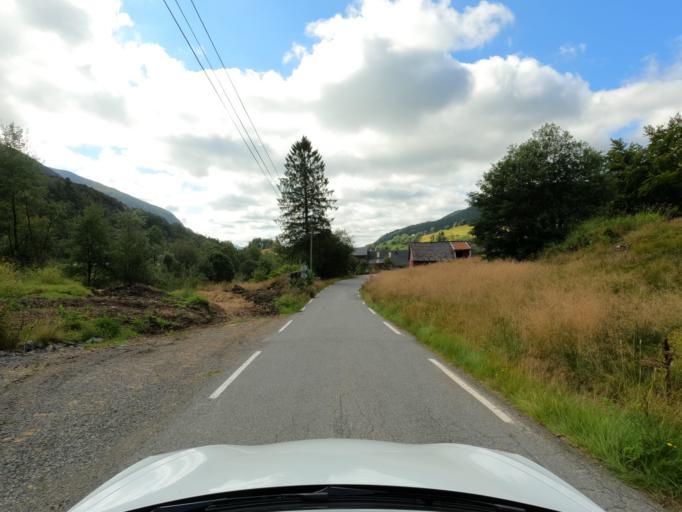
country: NO
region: Hordaland
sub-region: Bergen
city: Espeland
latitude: 60.3252
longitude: 5.5196
